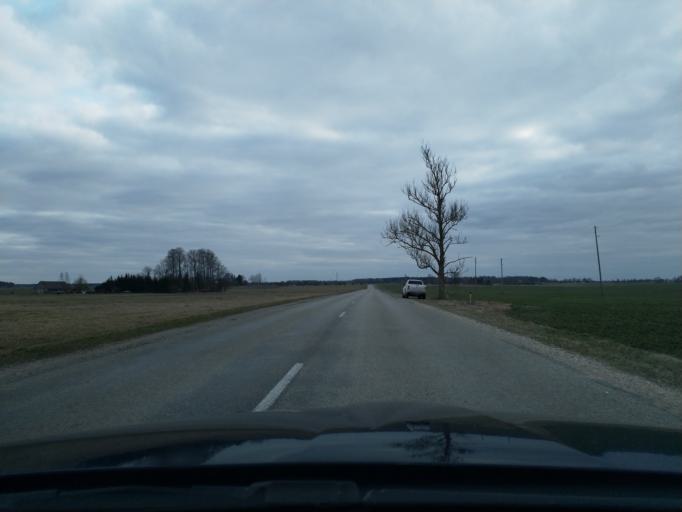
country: LV
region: Talsu Rajons
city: Sabile
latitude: 56.9523
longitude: 22.6079
